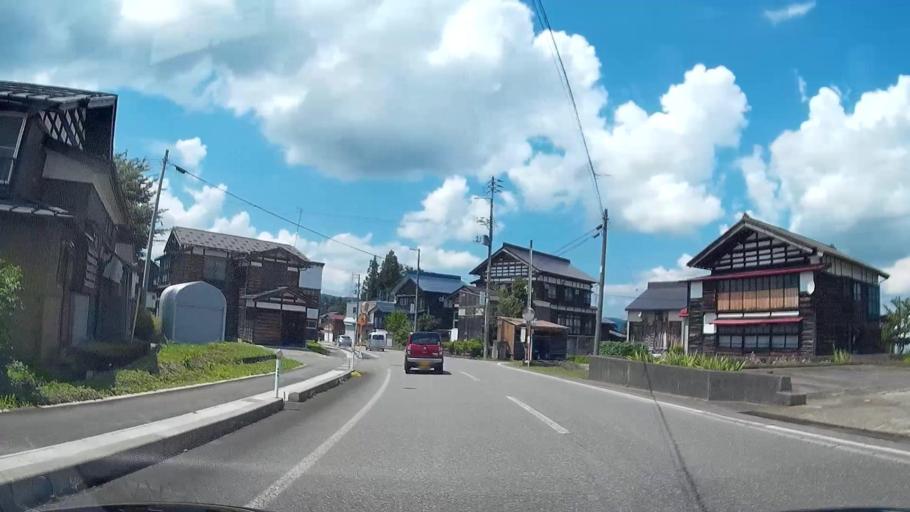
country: JP
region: Niigata
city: Tokamachi
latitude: 37.1004
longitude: 138.7374
